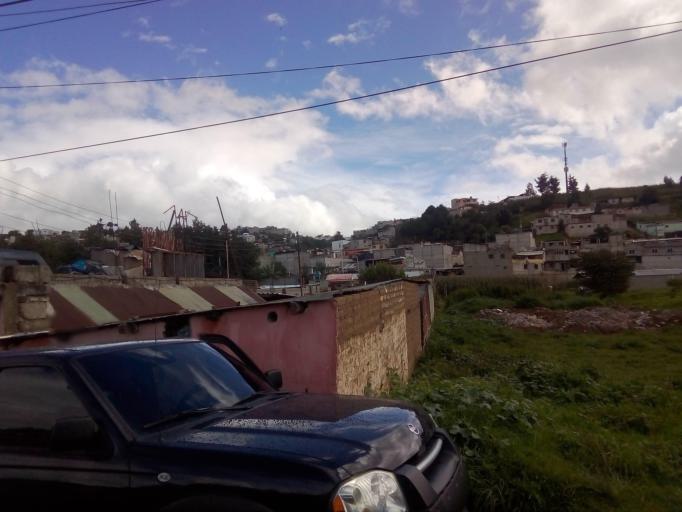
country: GT
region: Quetzaltenango
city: Quetzaltenango
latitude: 14.8475
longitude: -91.5100
